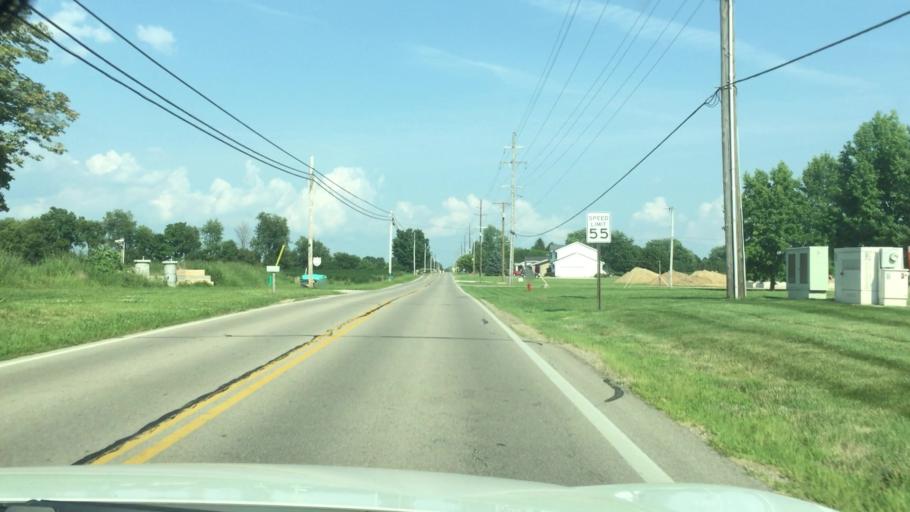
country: US
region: Ohio
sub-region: Clark County
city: Northridge
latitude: 39.9947
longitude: -83.7595
